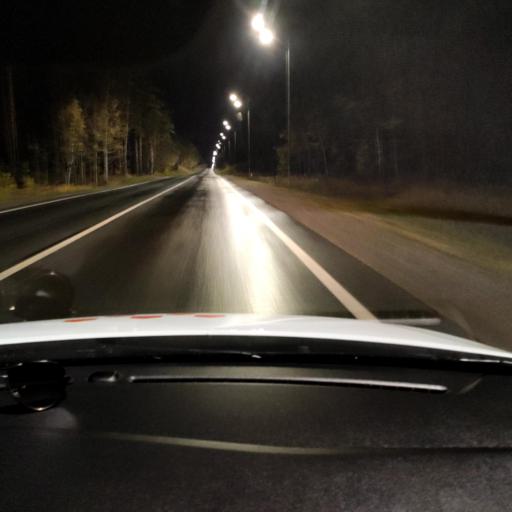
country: RU
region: Tatarstan
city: Verkhniy Uslon
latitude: 55.6390
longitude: 49.0353
